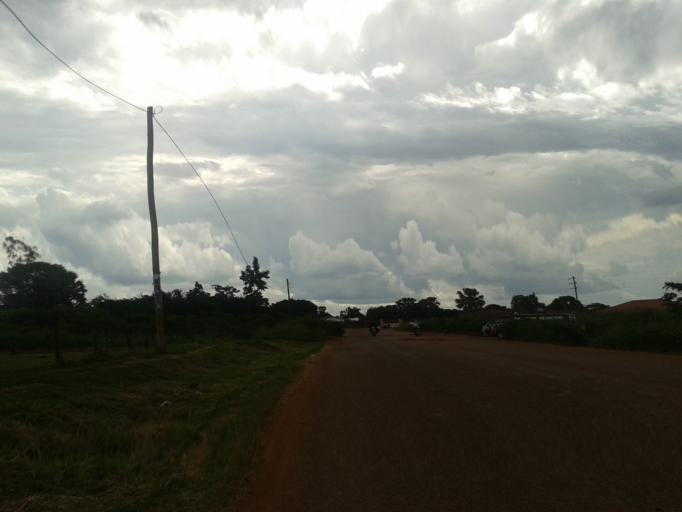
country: UG
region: Northern Region
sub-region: Gulu District
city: Gulu
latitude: 2.7846
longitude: 32.3087
